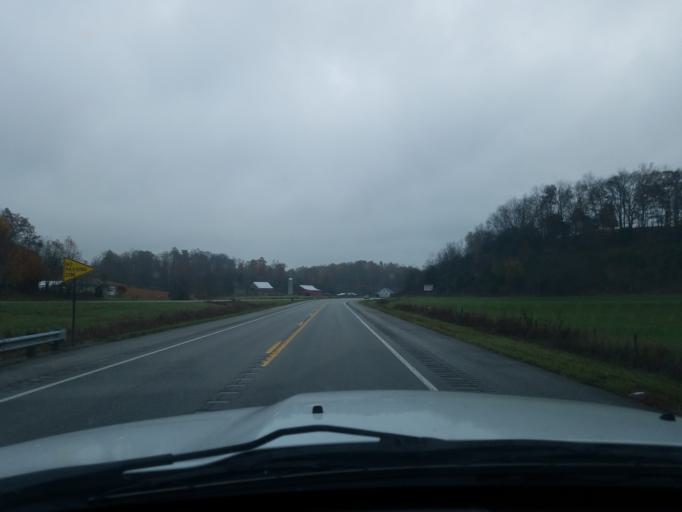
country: US
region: Kentucky
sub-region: Taylor County
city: Campbellsville
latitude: 37.3924
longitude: -85.4378
